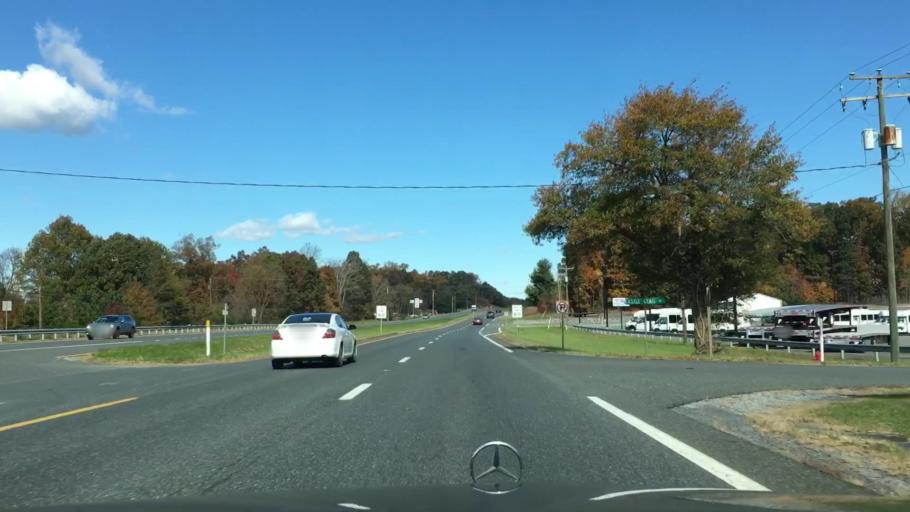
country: US
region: Virginia
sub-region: Campbell County
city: Altavista
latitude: 37.1993
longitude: -79.2034
